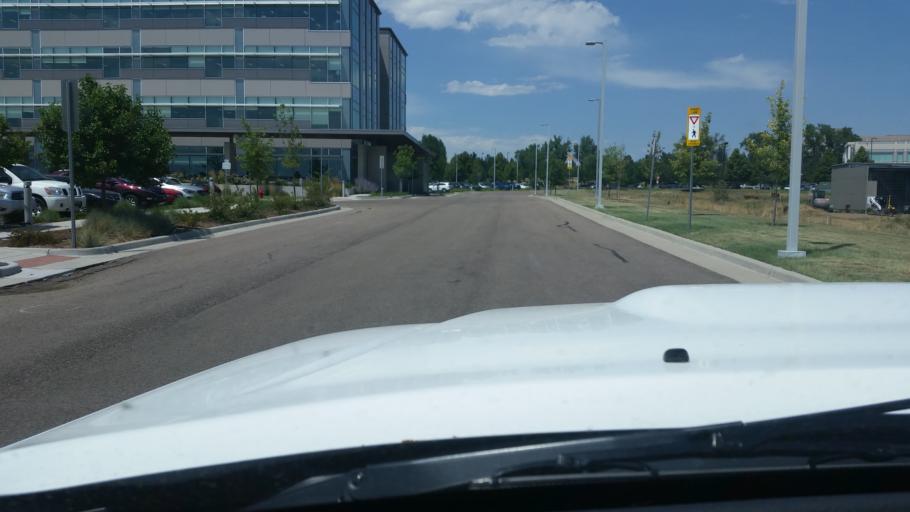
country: US
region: Colorado
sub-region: Broomfield County
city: Broomfield
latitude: 39.8964
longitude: -105.1148
